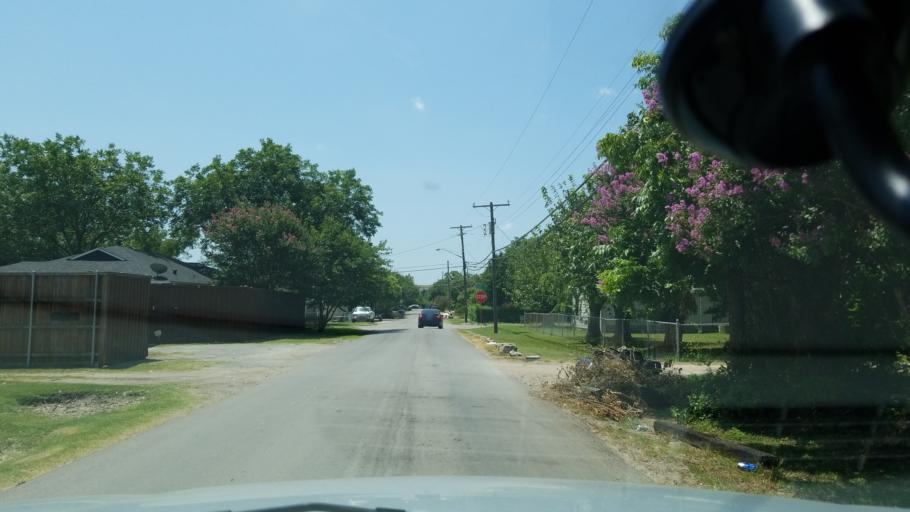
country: US
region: Texas
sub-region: Dallas County
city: Cockrell Hill
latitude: 32.7191
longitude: -96.8624
